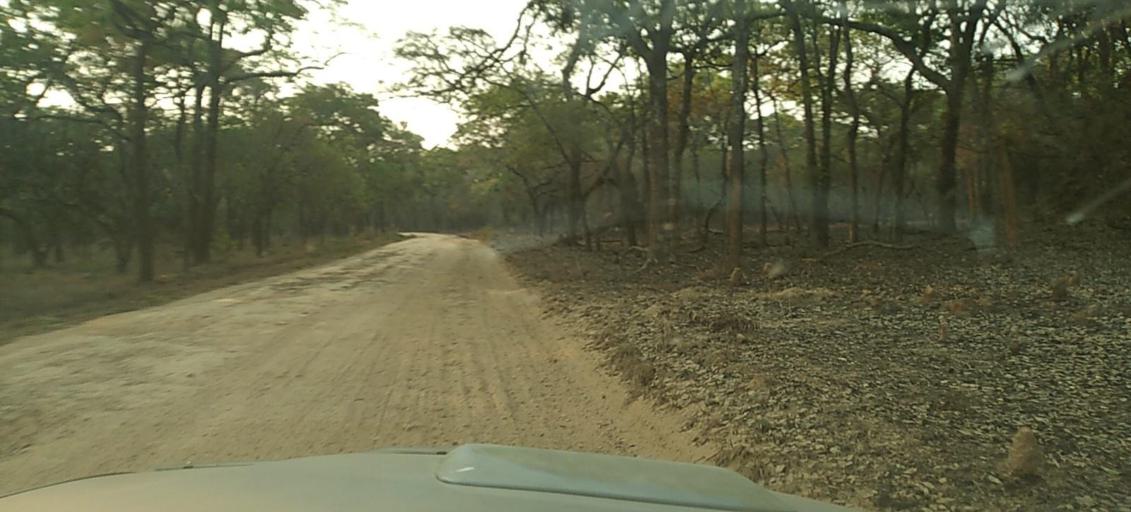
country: ZM
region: North-Western
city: Kasempa
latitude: -13.1585
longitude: 26.4491
